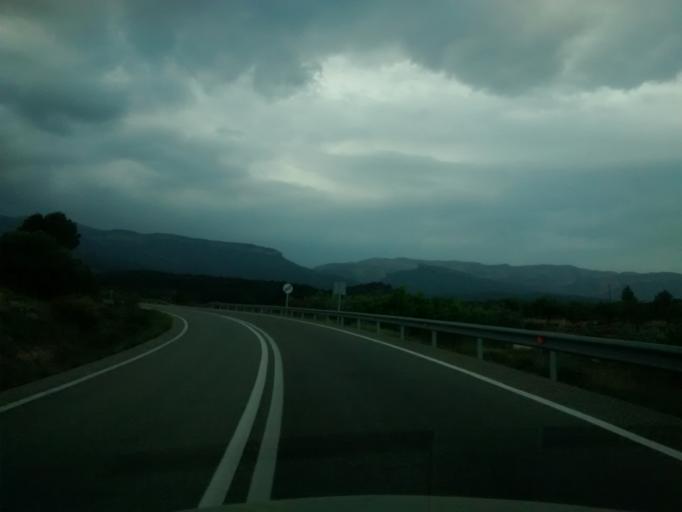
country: ES
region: Catalonia
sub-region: Provincia de Tarragona
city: Benifallet
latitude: 41.0032
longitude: 0.5135
